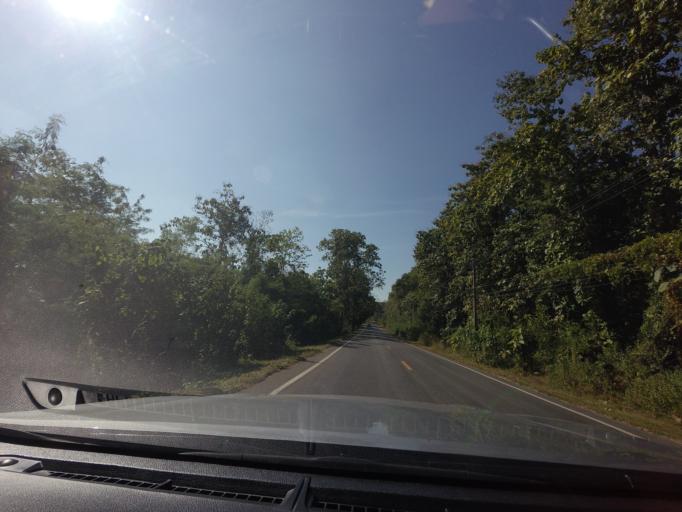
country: TH
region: Sukhothai
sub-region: Amphoe Si Satchanalai
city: Si Satchanalai
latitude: 17.6316
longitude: 99.6935
